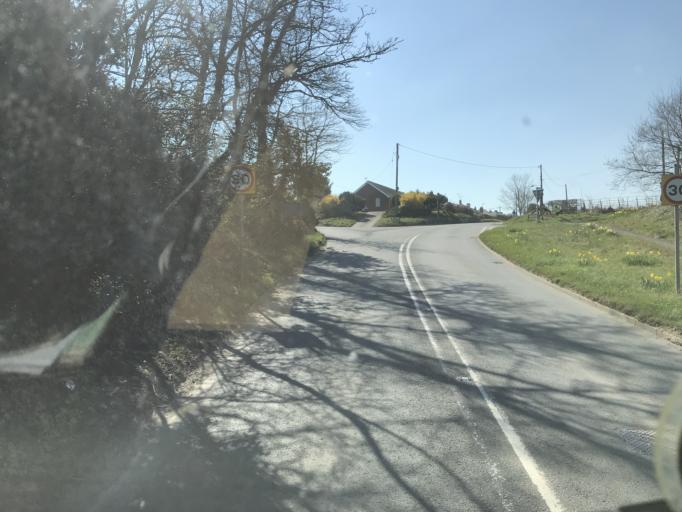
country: GB
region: Wales
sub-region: Wrexham
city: Gresford
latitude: 53.1045
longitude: -2.9755
